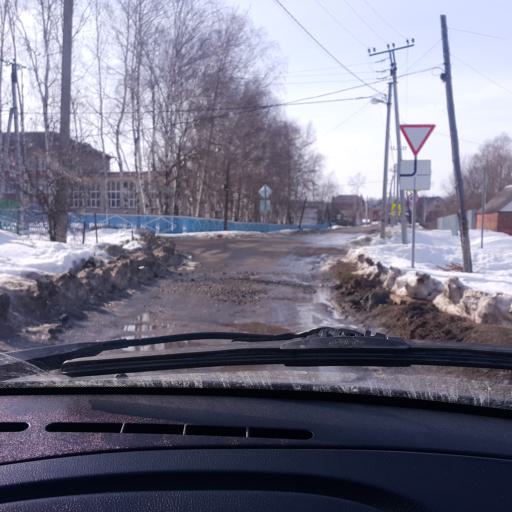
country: RU
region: Tambov
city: Sosnovka
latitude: 53.2389
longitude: 41.3684
